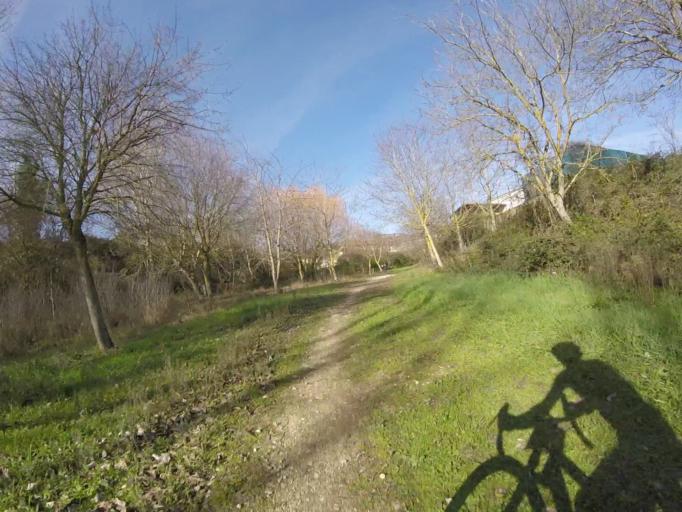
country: ES
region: Navarre
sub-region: Provincia de Navarra
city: Lezaun
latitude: 42.7268
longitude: -2.0145
